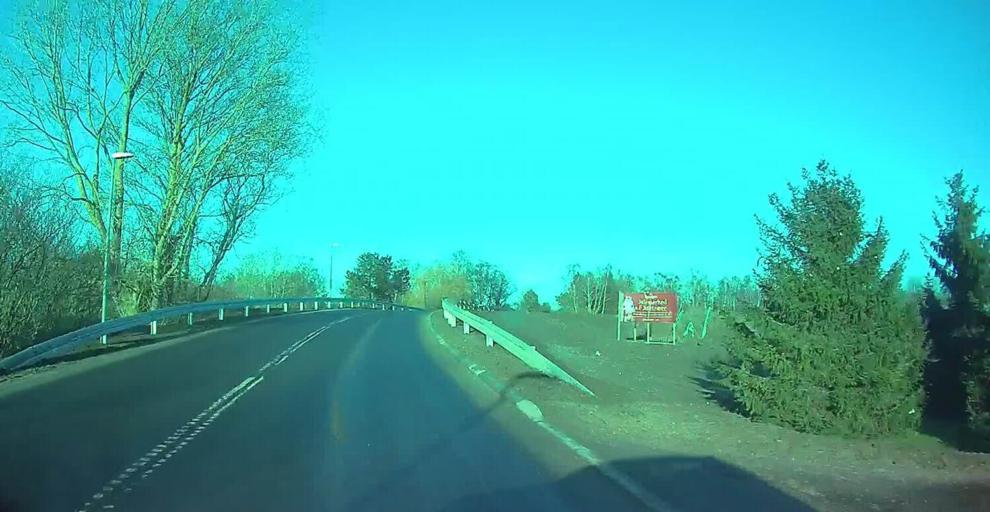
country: DK
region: Capital Region
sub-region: Tarnby Kommune
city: Tarnby
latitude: 55.5784
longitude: 12.5769
